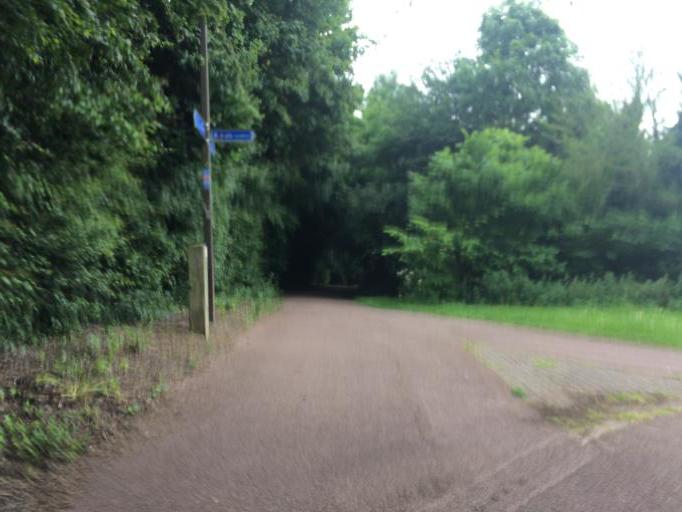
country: GB
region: England
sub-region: Milton Keynes
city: Loughton
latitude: 52.0324
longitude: -0.7744
